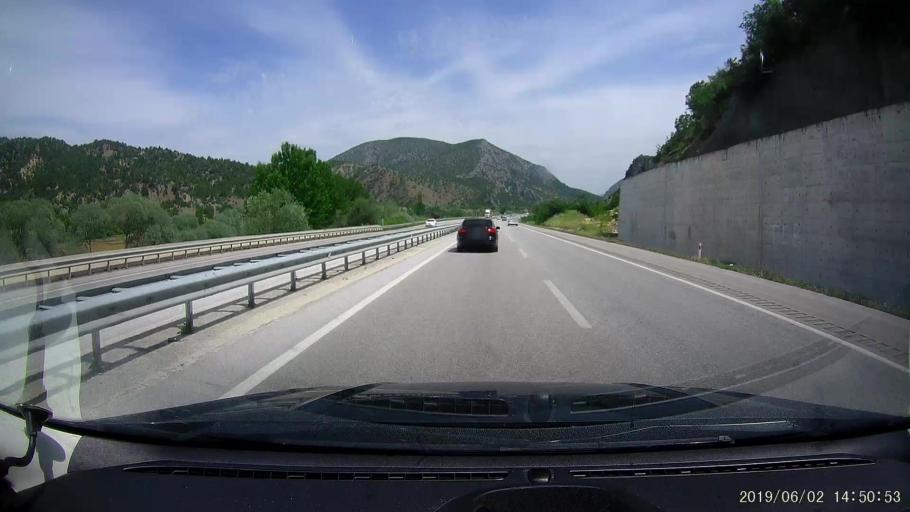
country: TR
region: Corum
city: Kargi
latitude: 41.0679
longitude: 34.5296
